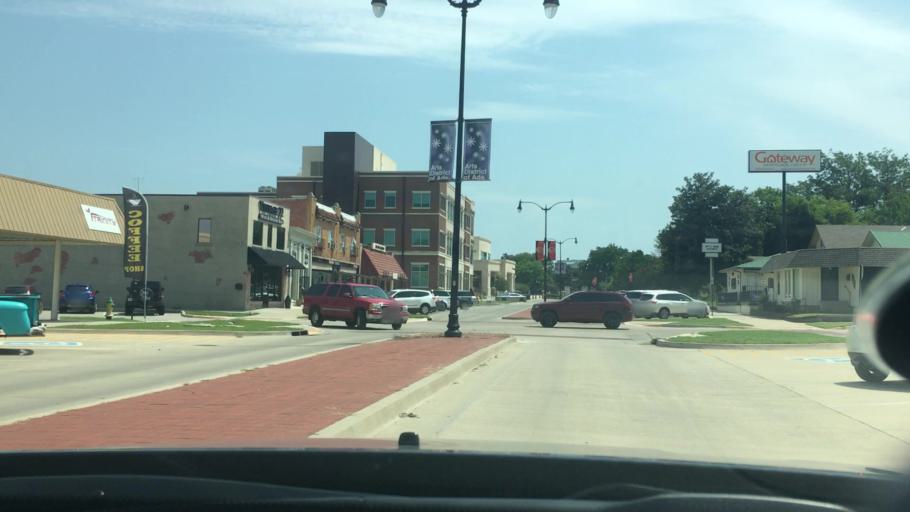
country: US
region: Oklahoma
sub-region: Pontotoc County
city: Ada
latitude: 34.7745
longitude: -96.6689
